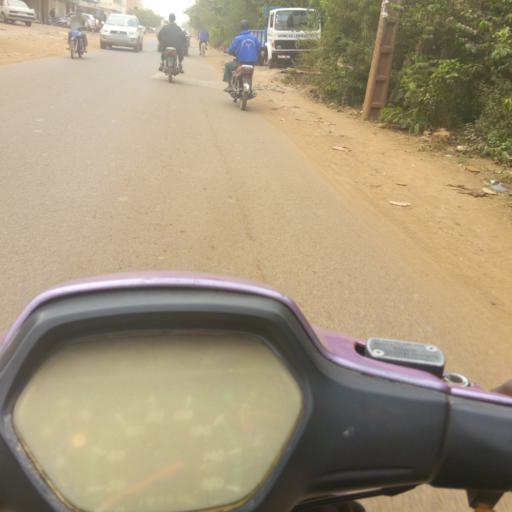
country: ML
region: Bamako
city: Bamako
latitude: 12.6633
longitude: -7.9359
